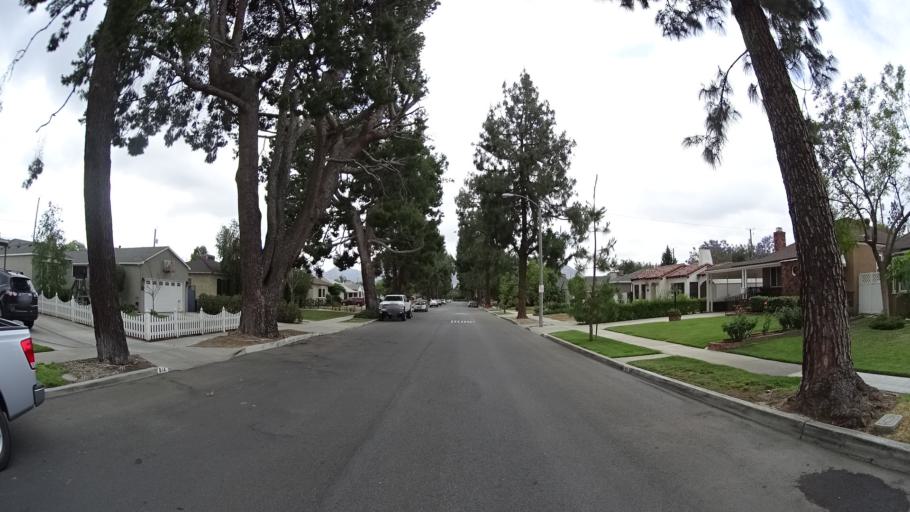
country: US
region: California
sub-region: Los Angeles County
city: Burbank
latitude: 34.1691
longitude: -118.3393
